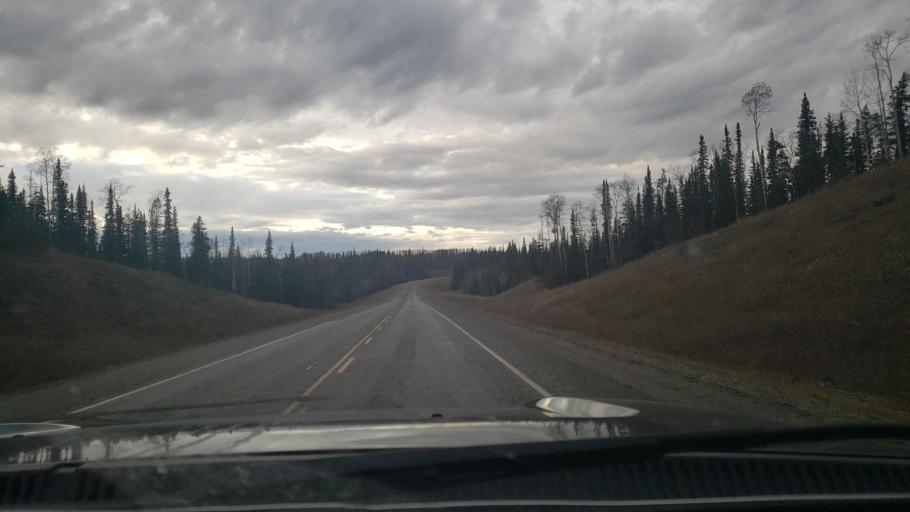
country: CA
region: Yukon
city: Watson Lake
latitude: 59.9821
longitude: -127.5835
